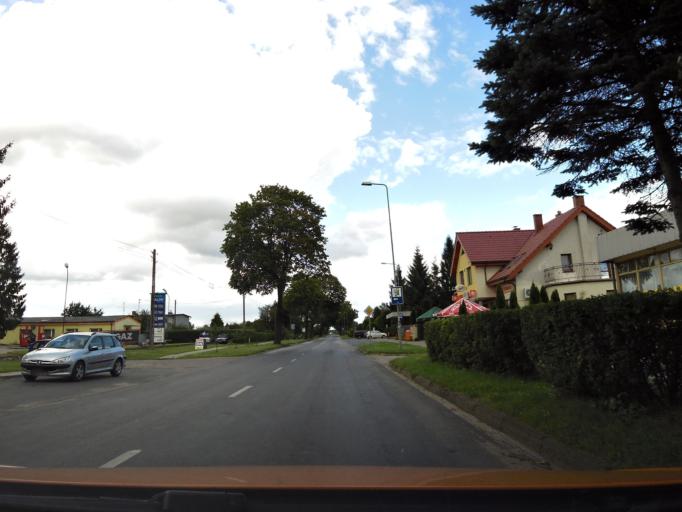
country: PL
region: West Pomeranian Voivodeship
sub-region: Powiat kolobrzeski
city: Ryman
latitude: 54.0298
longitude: 15.5373
